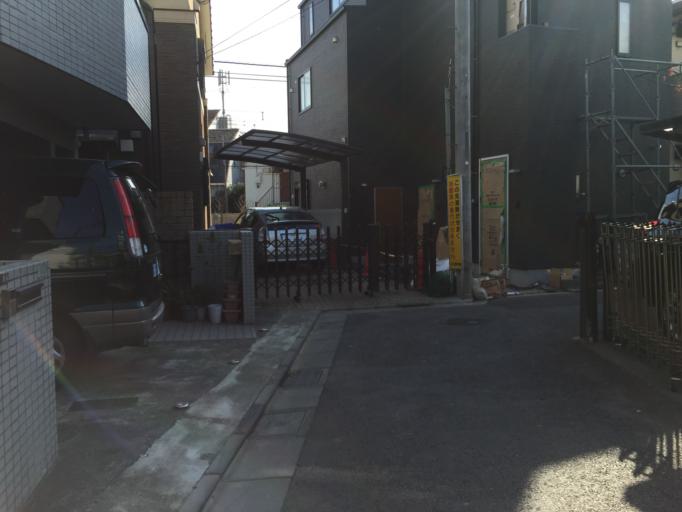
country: JP
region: Tokyo
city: Tokyo
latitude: 35.6670
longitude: 139.6450
